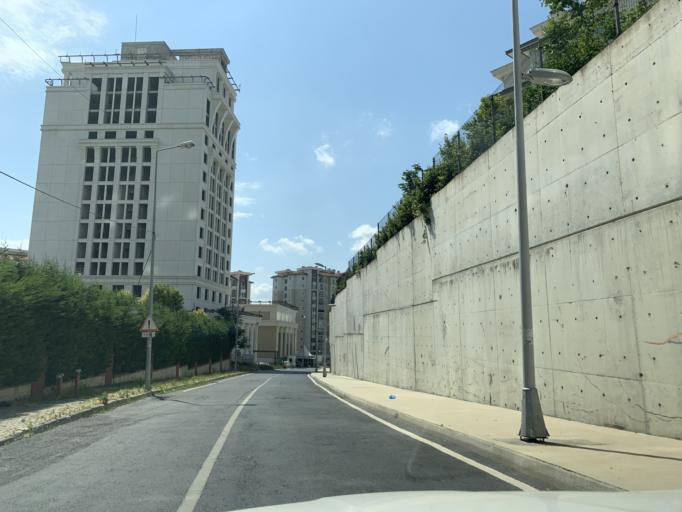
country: TR
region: Istanbul
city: Esenyurt
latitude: 41.0738
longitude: 28.6981
